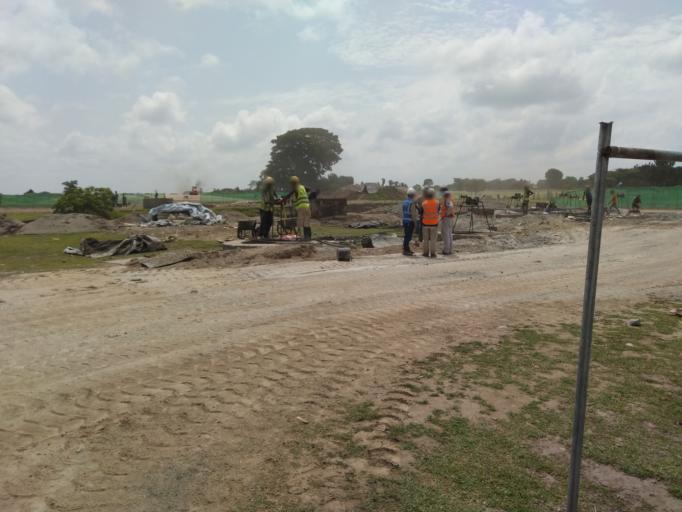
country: ET
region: Oromiya
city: Shashemene
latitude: 7.2699
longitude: 38.5988
